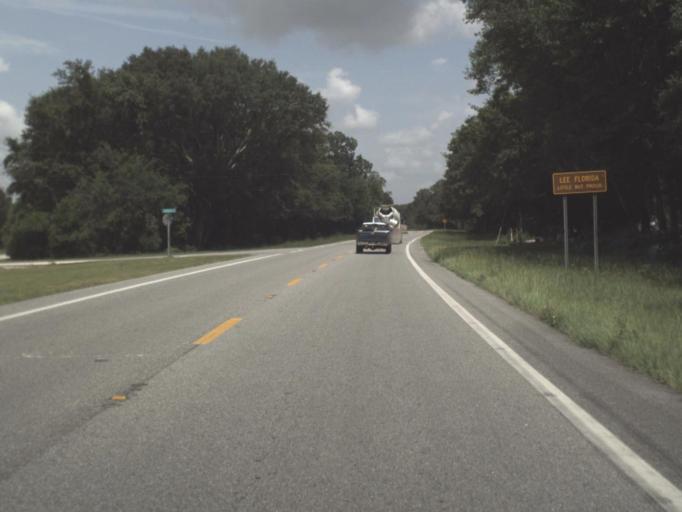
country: US
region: Florida
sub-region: Madison County
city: Madison
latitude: 30.4173
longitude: -83.2922
